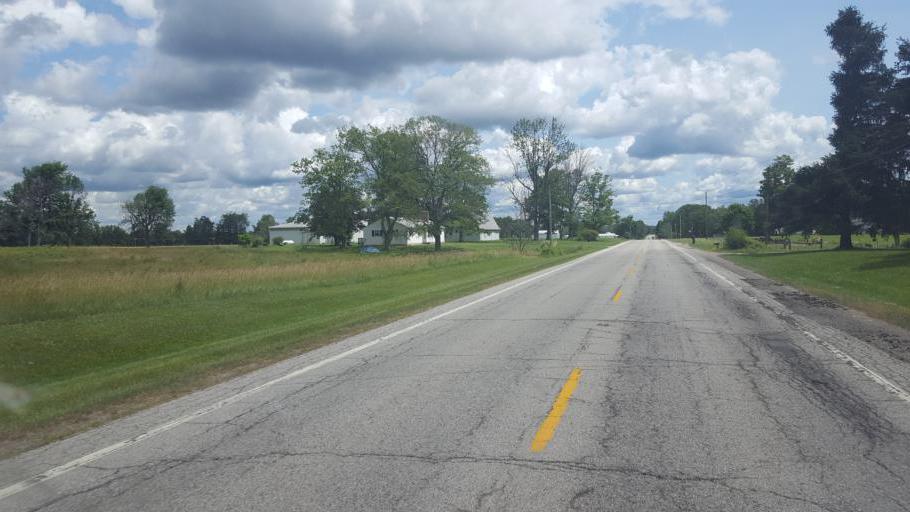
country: US
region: Ohio
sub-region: Richland County
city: Lexington
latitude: 40.6126
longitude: -82.6766
